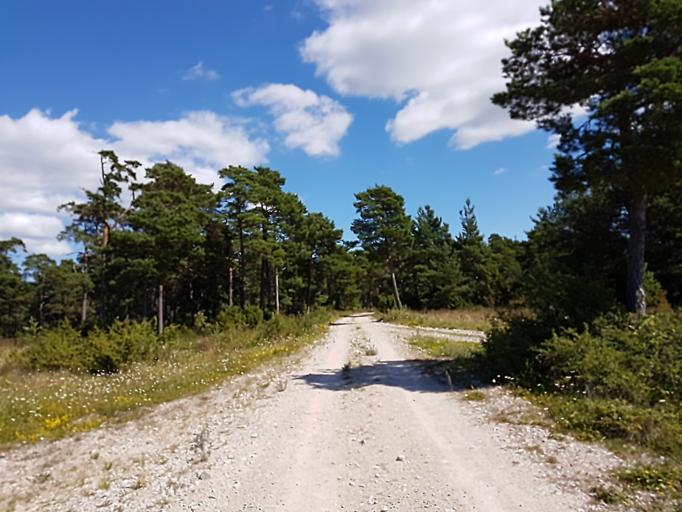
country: SE
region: Gotland
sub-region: Gotland
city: Visby
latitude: 57.6088
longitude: 18.3322
